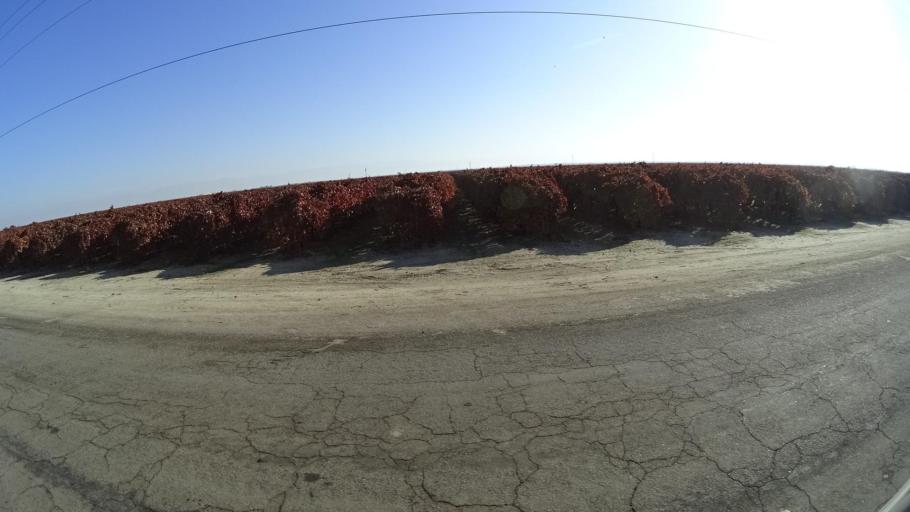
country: US
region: California
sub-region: Kern County
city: McFarland
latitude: 35.7354
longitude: -119.1695
